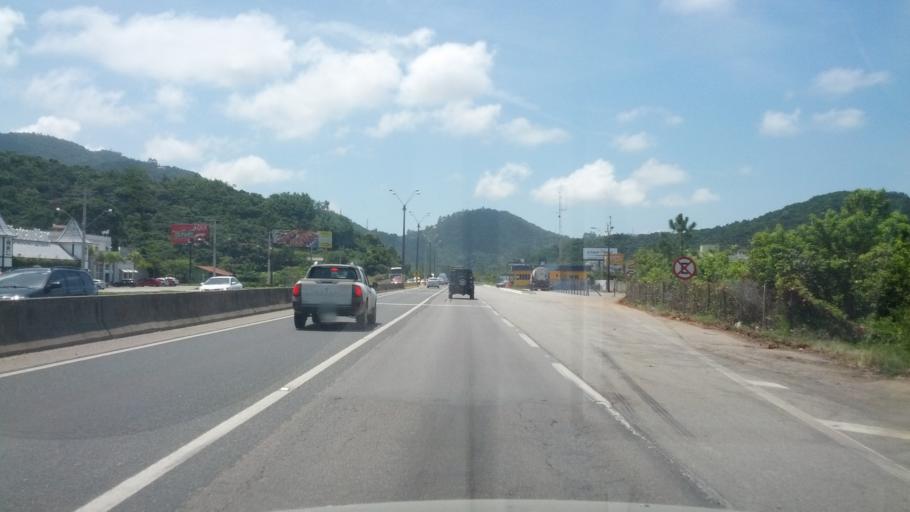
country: BR
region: Santa Catarina
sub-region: Itapema
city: Itapema
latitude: -27.0676
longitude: -48.5956
